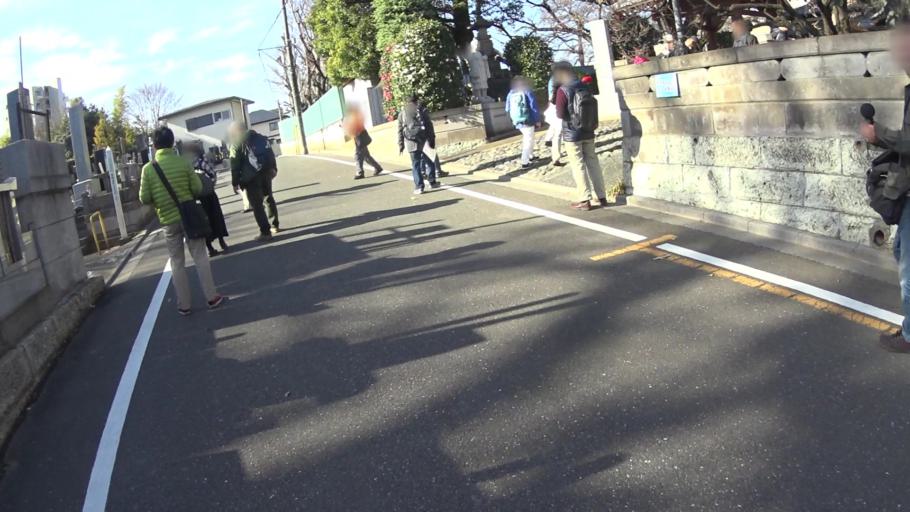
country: JP
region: Saitama
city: Yono
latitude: 35.8491
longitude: 139.6486
